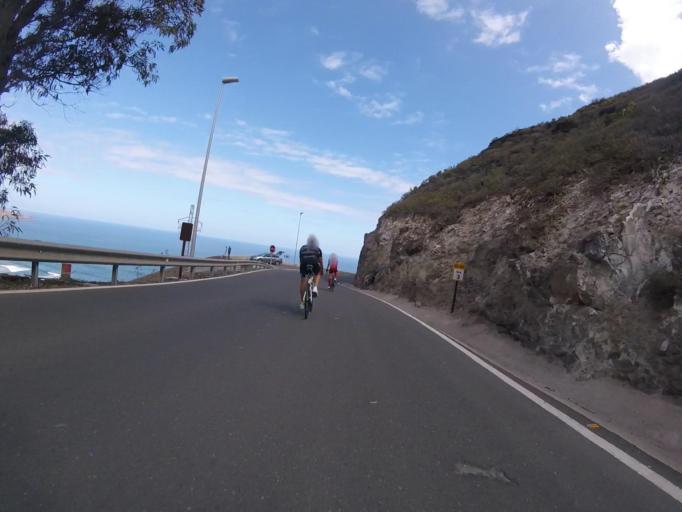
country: ES
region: Canary Islands
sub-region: Provincia de Las Palmas
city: Guia
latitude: 28.1412
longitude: -15.5933
